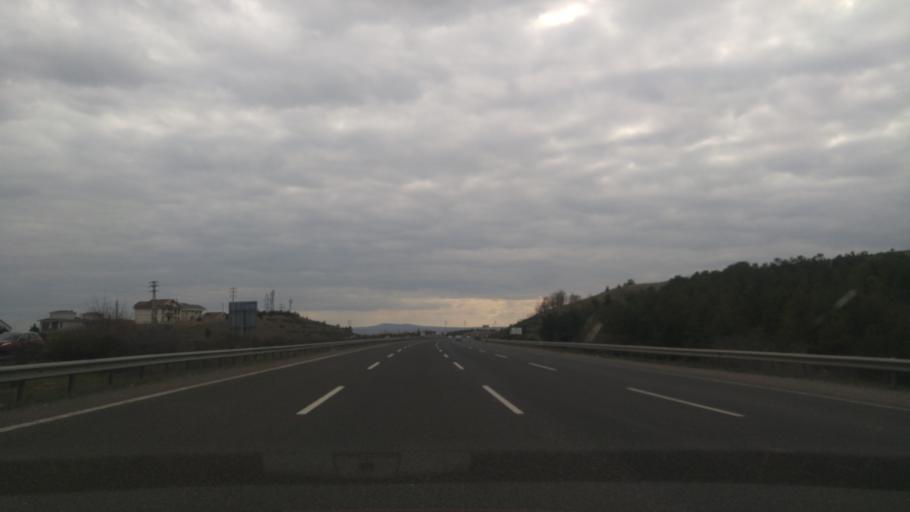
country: TR
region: Ankara
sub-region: Goelbasi
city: Golbasi
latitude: 39.7980
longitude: 32.7896
